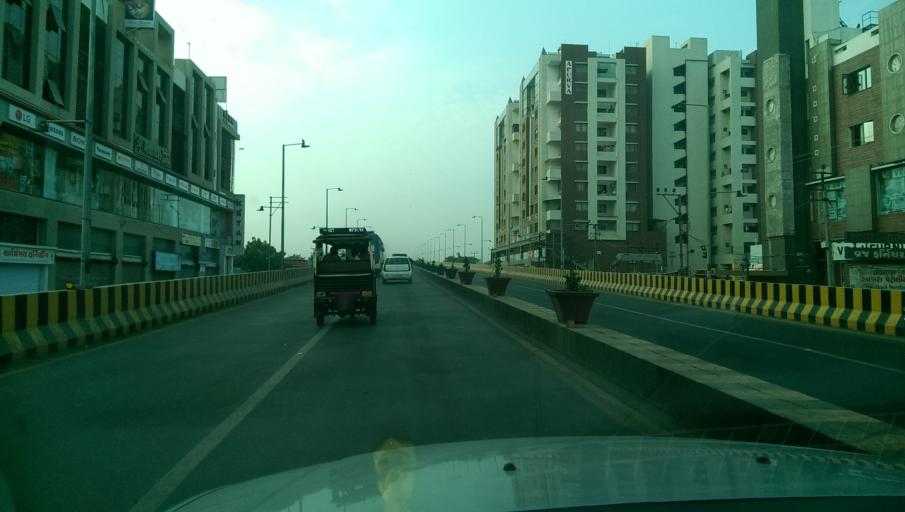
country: IN
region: Gujarat
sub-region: Jamnagar
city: Jamnagar
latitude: 22.4694
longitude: 70.0418
